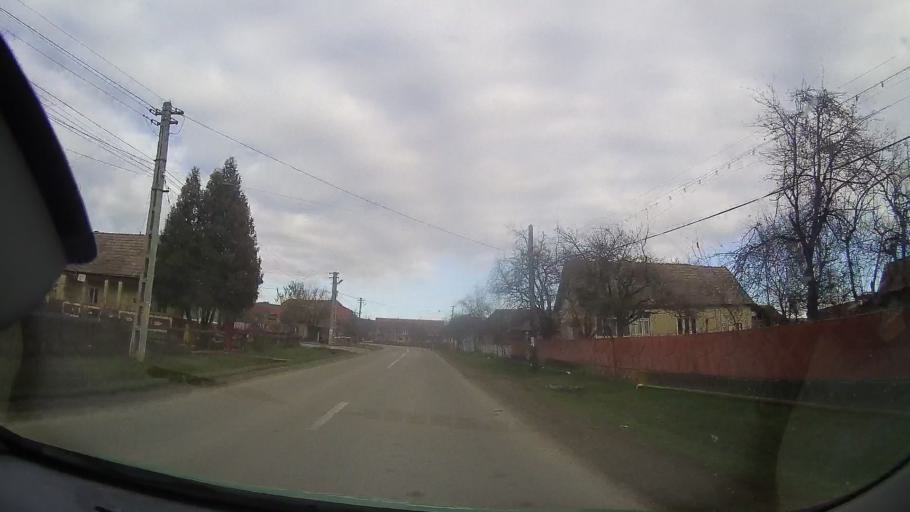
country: RO
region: Mures
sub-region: Comuna Iernut
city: Iernut
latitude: 46.4759
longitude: 24.2277
